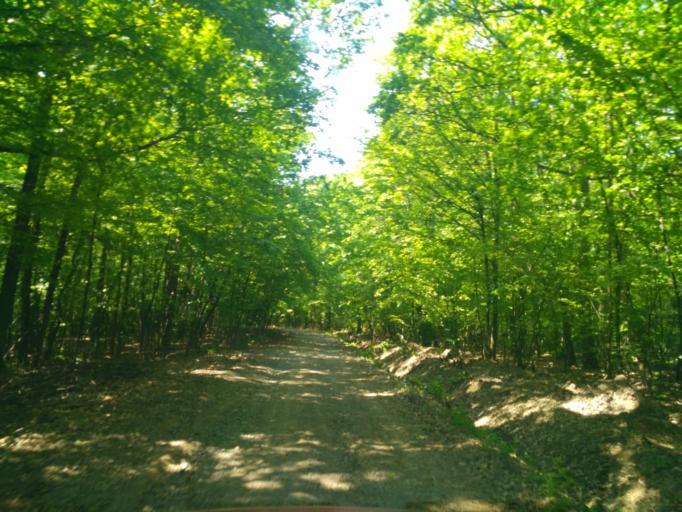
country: SK
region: Kosicky
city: Kosice
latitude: 48.8376
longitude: 21.4555
